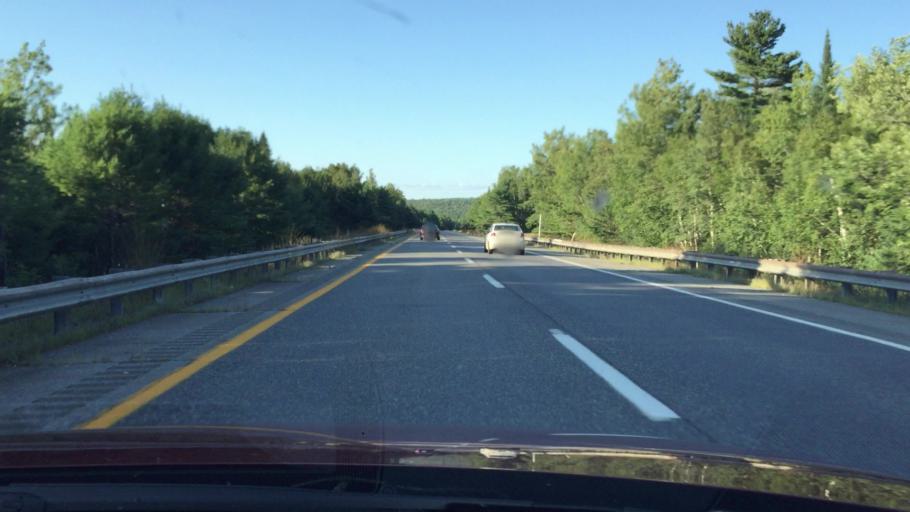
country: US
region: Maine
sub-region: Penobscot County
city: Medway
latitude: 45.6238
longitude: -68.5071
